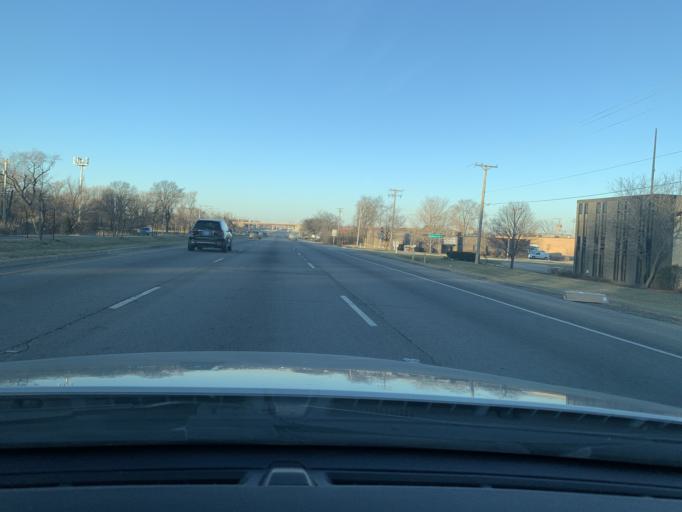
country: US
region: Illinois
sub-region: DuPage County
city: Wood Dale
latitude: 41.9758
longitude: -87.9591
